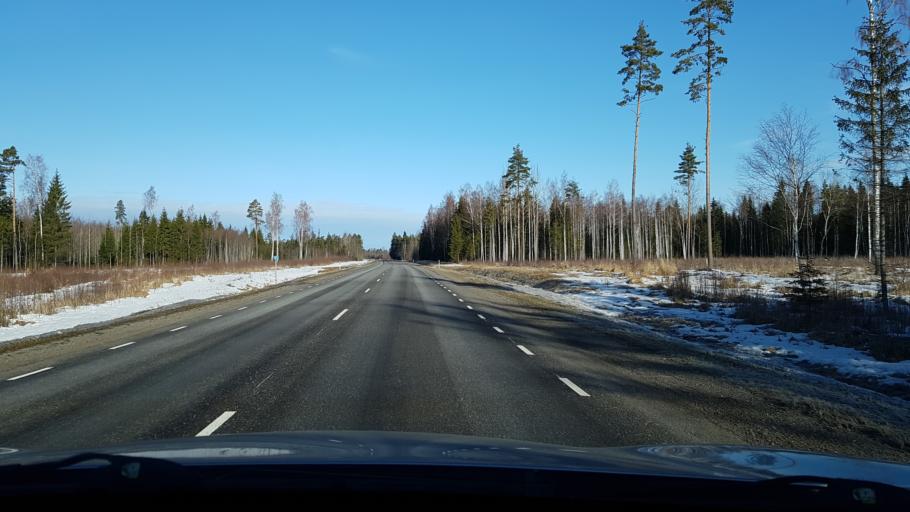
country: EE
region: Viljandimaa
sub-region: Vohma linn
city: Vohma
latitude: 58.6055
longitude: 25.5725
